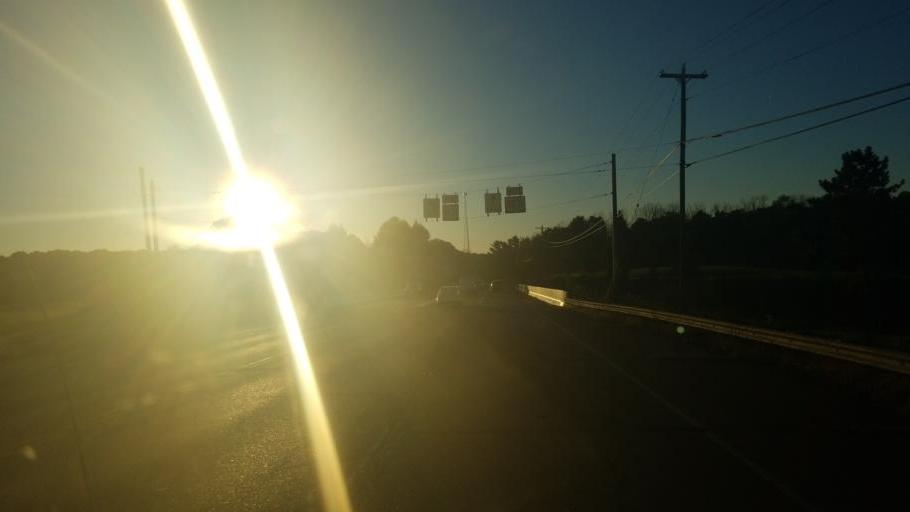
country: US
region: Ohio
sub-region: Stark County
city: Alliance
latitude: 40.9022
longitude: -81.1688
